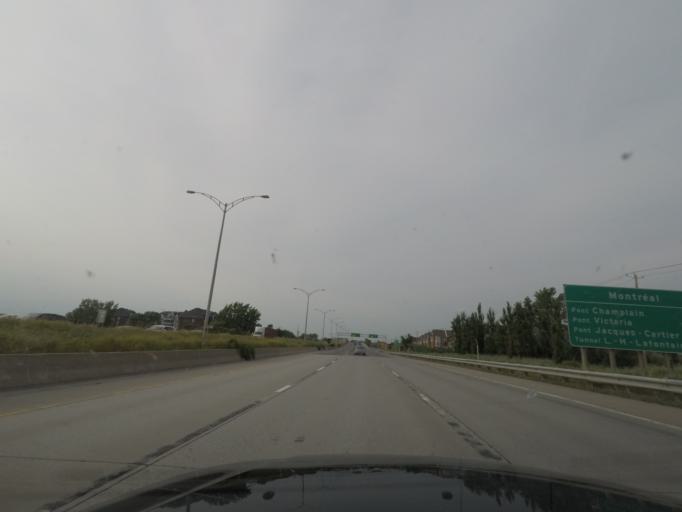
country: CA
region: Quebec
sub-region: Monteregie
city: La Prairie
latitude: 45.4306
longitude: -73.4904
